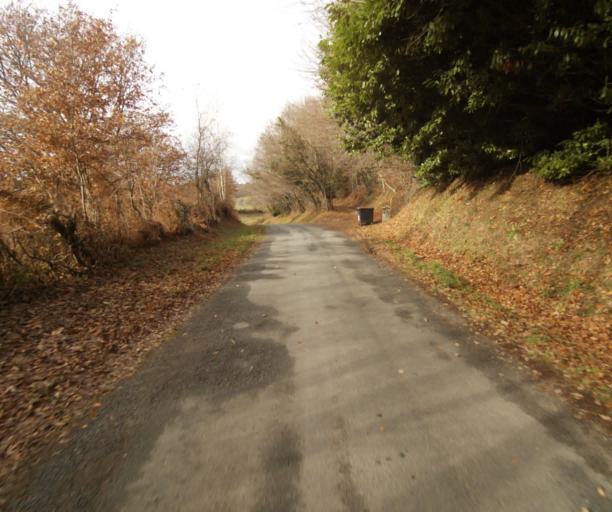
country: FR
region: Limousin
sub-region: Departement de la Correze
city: Chameyrat
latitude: 45.2565
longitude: 1.6966
